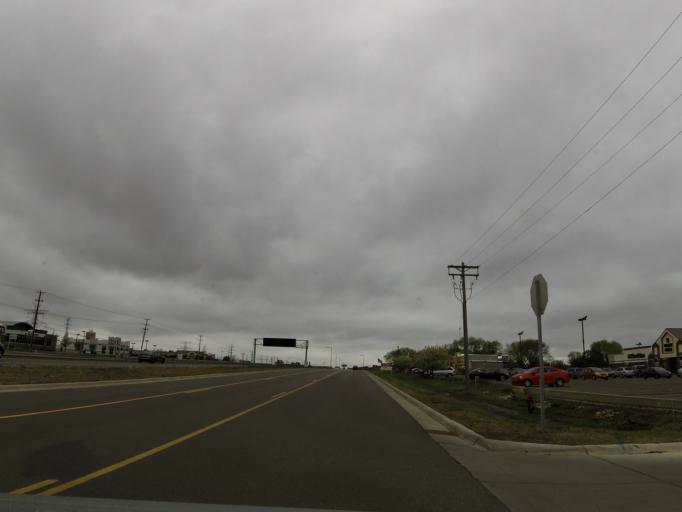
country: US
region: Minnesota
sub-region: Washington County
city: Stillwater
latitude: 45.0363
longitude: -92.8257
